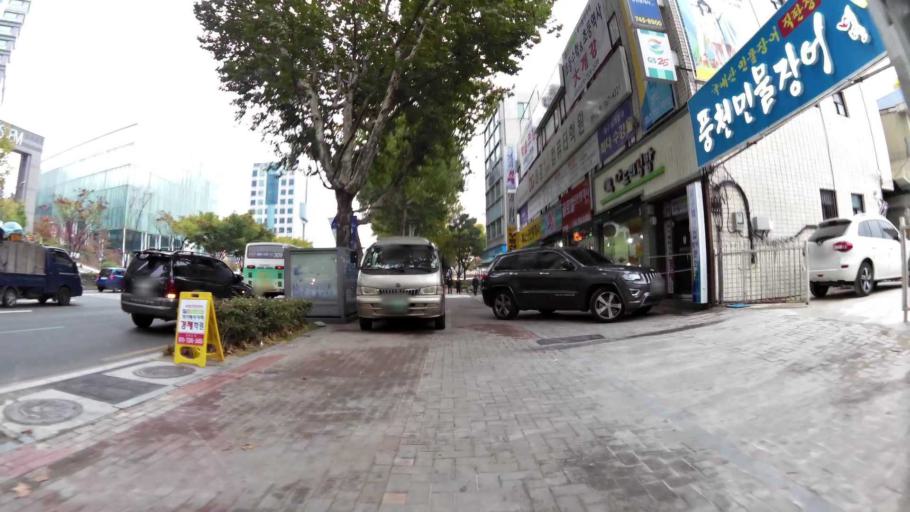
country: KR
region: Daegu
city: Daegu
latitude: 35.8587
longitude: 128.6294
